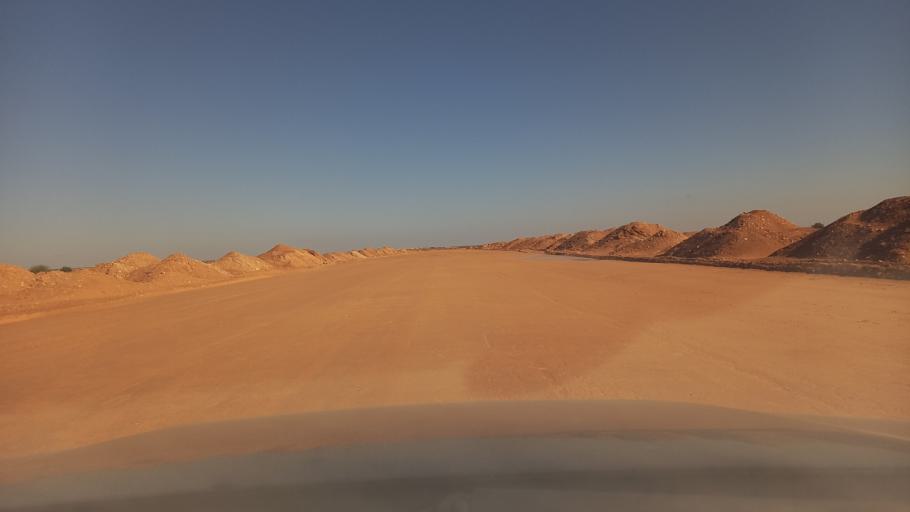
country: TN
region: Madanin
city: Medenine
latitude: 33.1634
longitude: 10.5206
